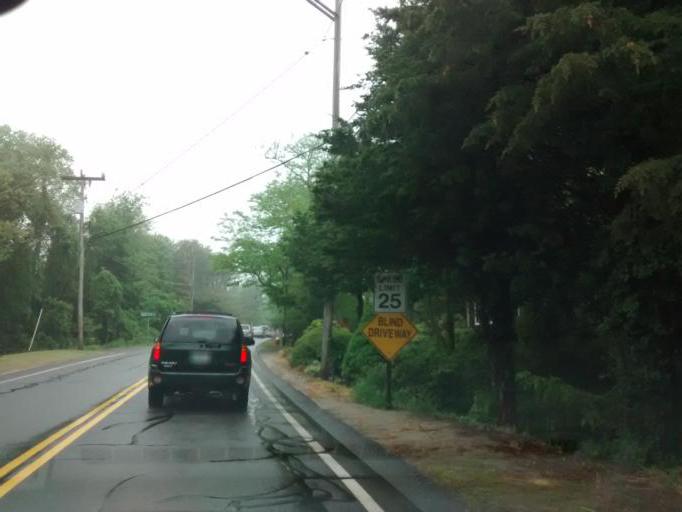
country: US
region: Massachusetts
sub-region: Barnstable County
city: Pocasset
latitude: 41.6921
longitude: -70.6040
